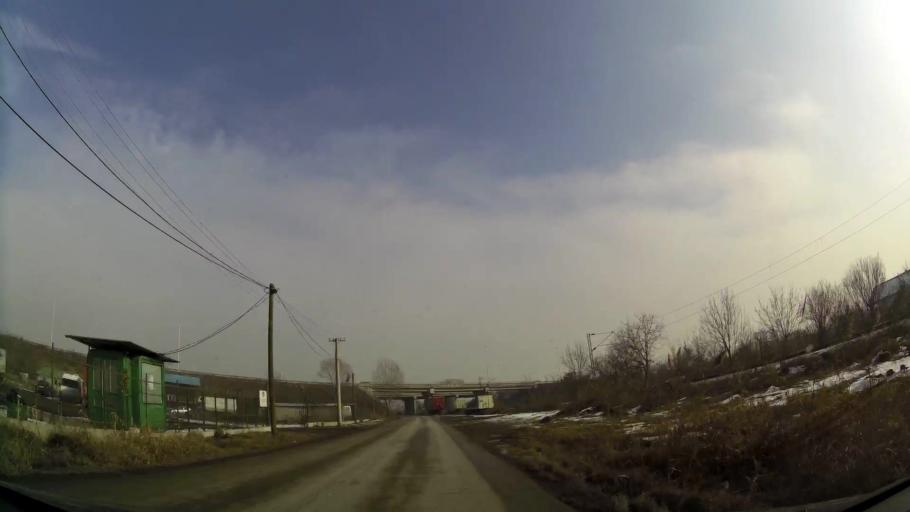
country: MK
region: Ilinden
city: Jurumleri
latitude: 41.9912
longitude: 21.5331
